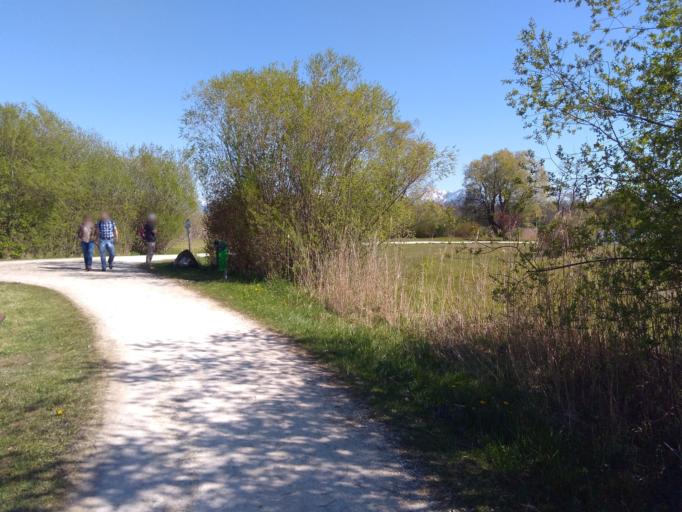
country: DE
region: Bavaria
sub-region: Upper Bavaria
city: Chiemsee
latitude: 47.8760
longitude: 12.3884
